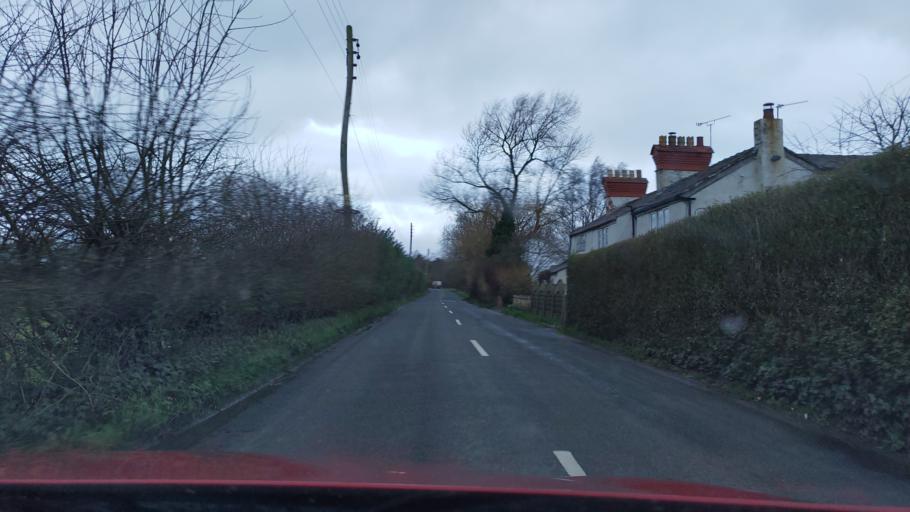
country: GB
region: England
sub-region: Lancashire
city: Ormskirk
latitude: 53.6240
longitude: -2.8660
